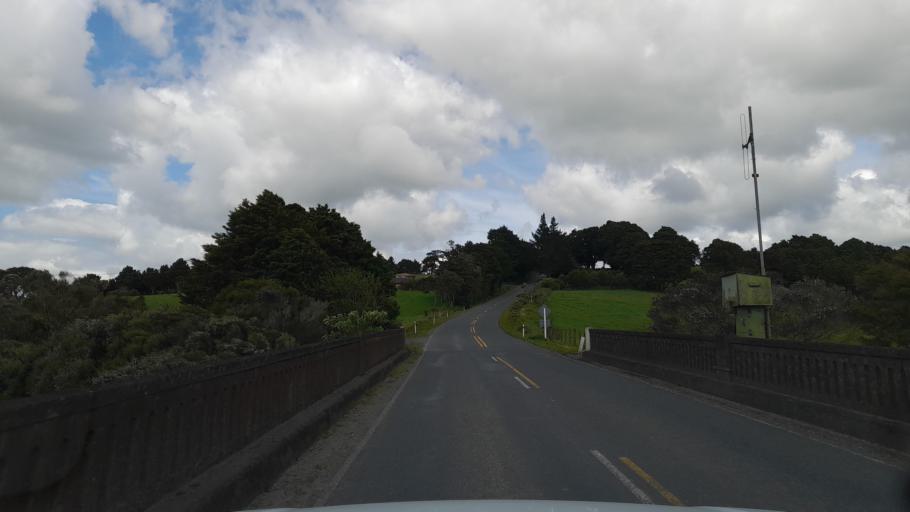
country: NZ
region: Northland
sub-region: Whangarei
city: Maungatapere
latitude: -35.6526
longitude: 174.1519
